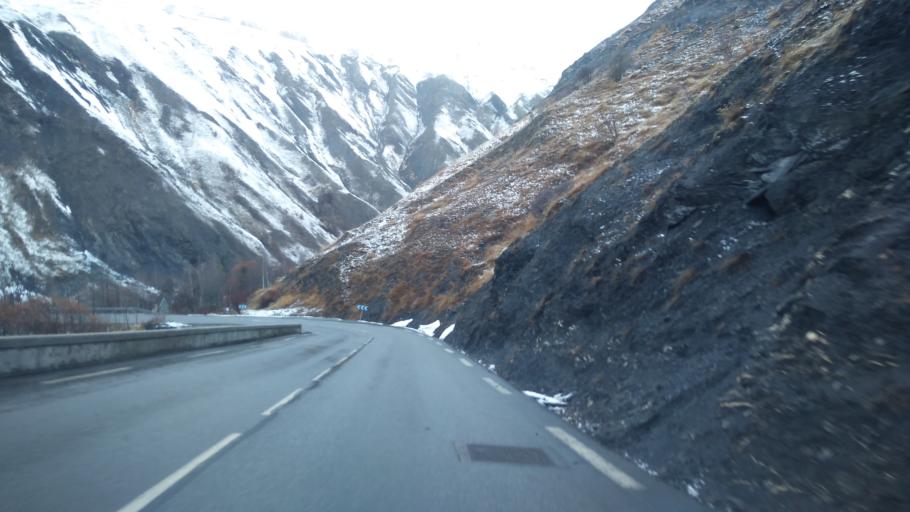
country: FR
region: Rhone-Alpes
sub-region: Departement de la Savoie
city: Valloire
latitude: 45.0485
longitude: 6.3162
